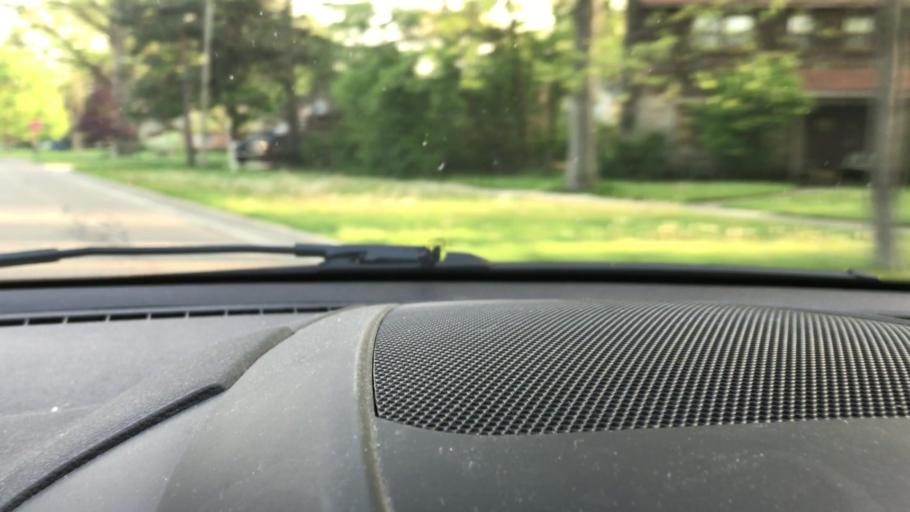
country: US
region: Michigan
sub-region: Oakland County
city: Huntington Woods
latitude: 42.4811
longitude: -83.1731
